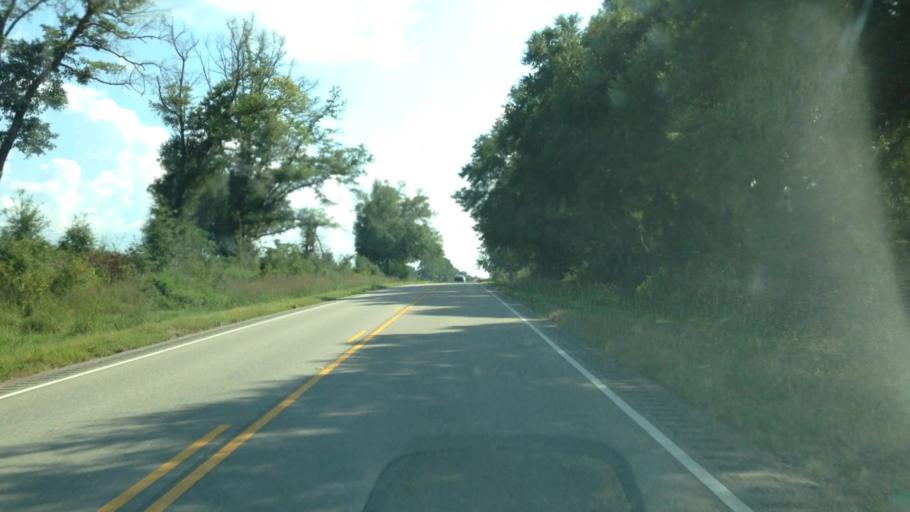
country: US
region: Alabama
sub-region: Covington County
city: Andalusia
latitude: 31.0713
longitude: -86.5753
